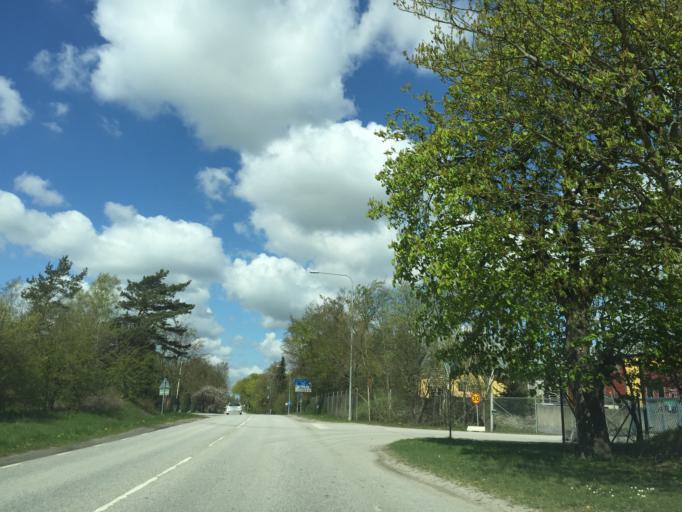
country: SE
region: Skane
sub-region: Lunds Kommun
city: Genarp
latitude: 55.6952
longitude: 13.3502
